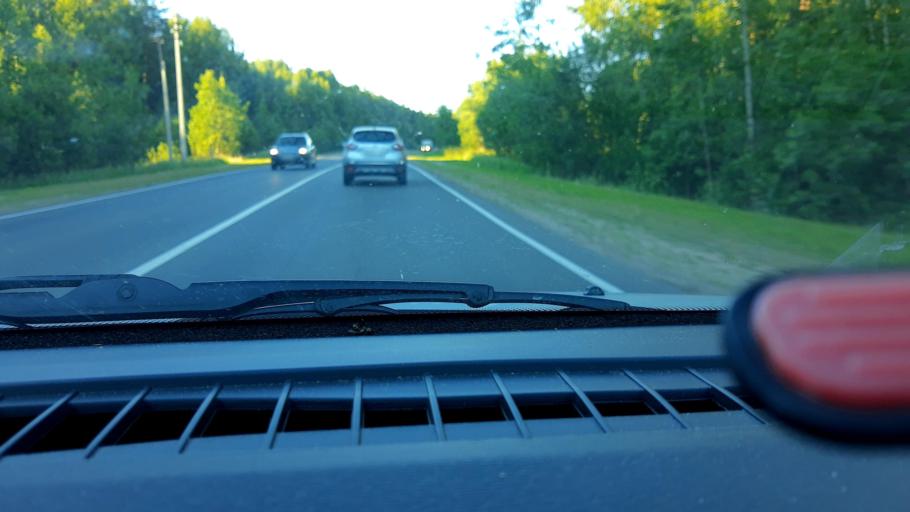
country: RU
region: Nizjnij Novgorod
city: Semenov
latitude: 56.8060
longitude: 44.4632
